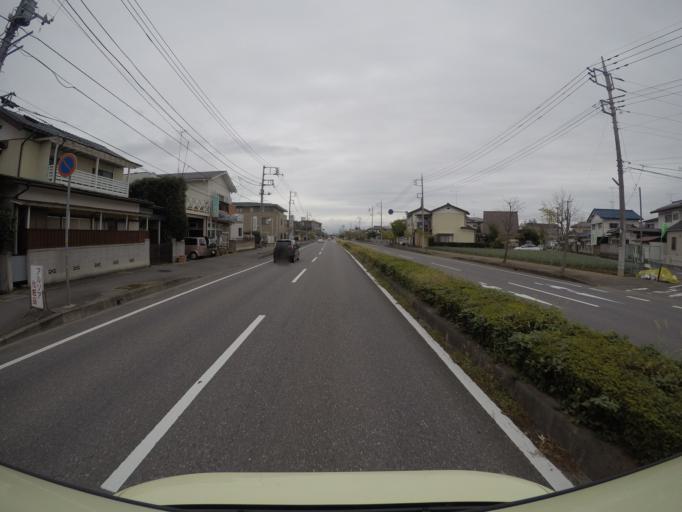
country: JP
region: Ibaraki
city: Naka
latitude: 36.0877
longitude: 140.1914
